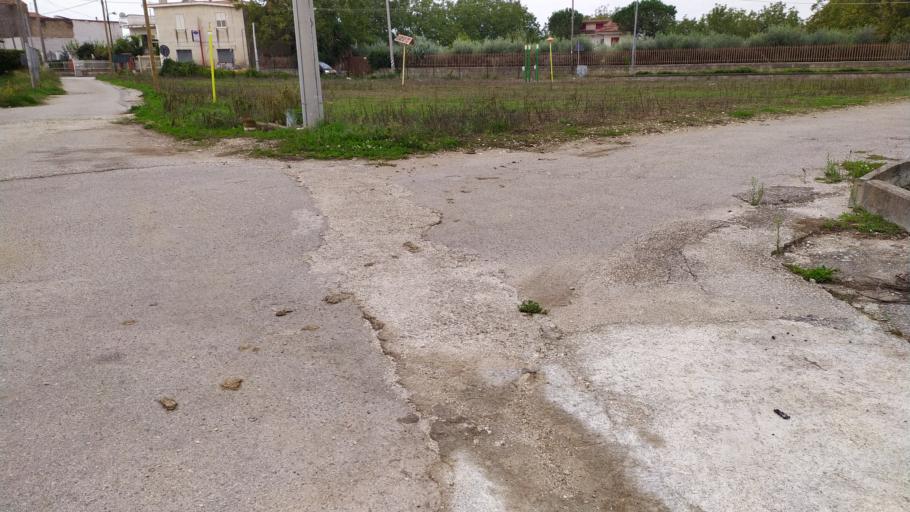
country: IT
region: Campania
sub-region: Provincia di Caserta
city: Montedecoro
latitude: 41.0012
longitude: 14.4140
